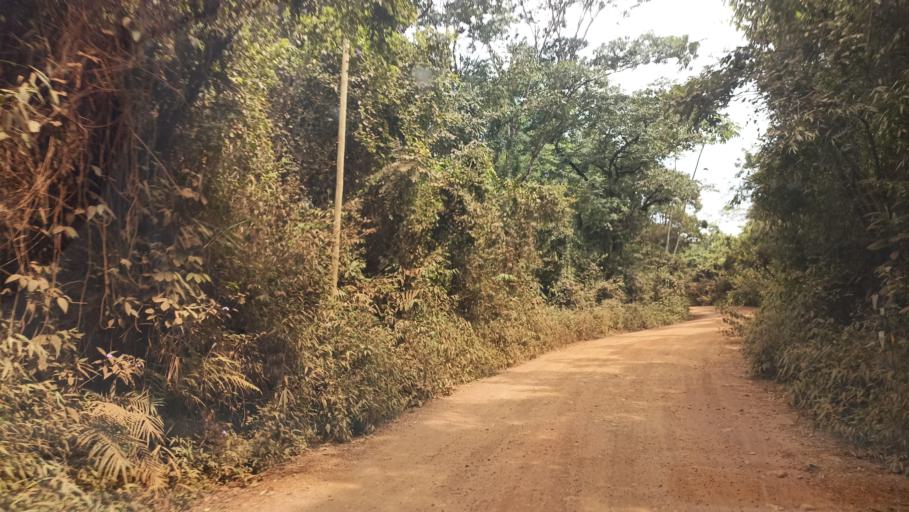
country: BR
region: Minas Gerais
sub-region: Itabirito
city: Itabirito
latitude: -20.3724
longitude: -43.7615
